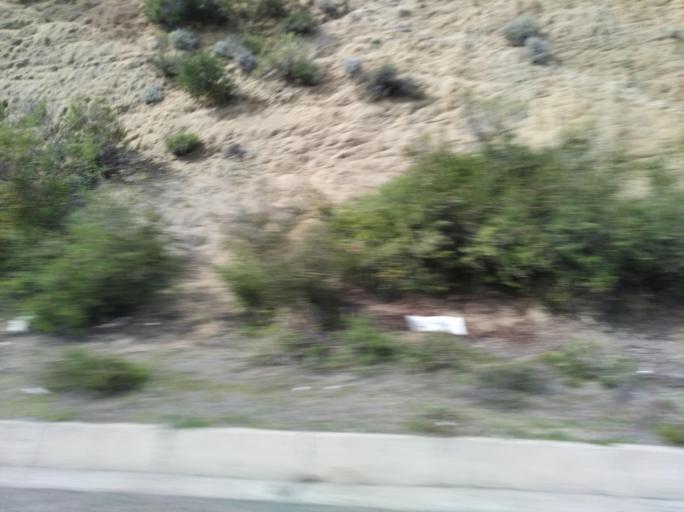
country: CL
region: Valparaiso
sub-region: Provincia de San Felipe
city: Llaillay
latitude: -33.0637
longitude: -71.0169
